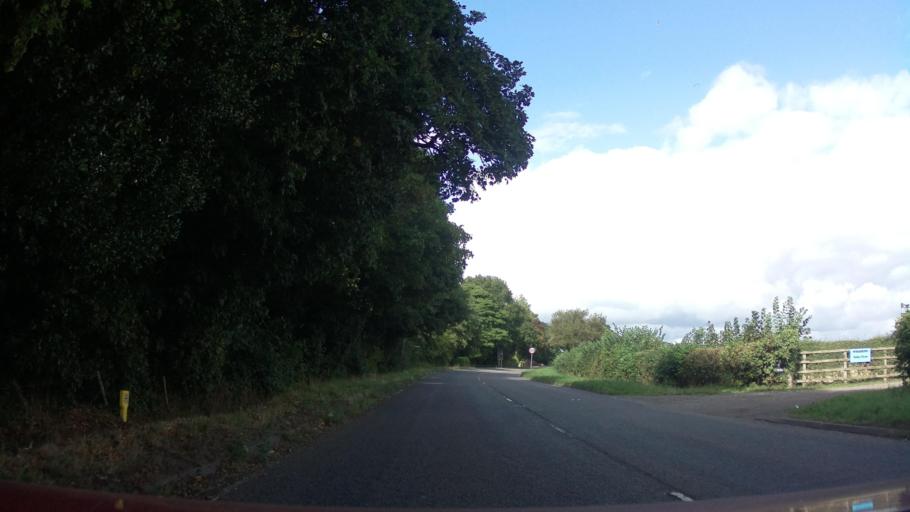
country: GB
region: England
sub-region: Leicestershire
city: Ashby de la Zouch
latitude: 52.7310
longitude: -1.4865
